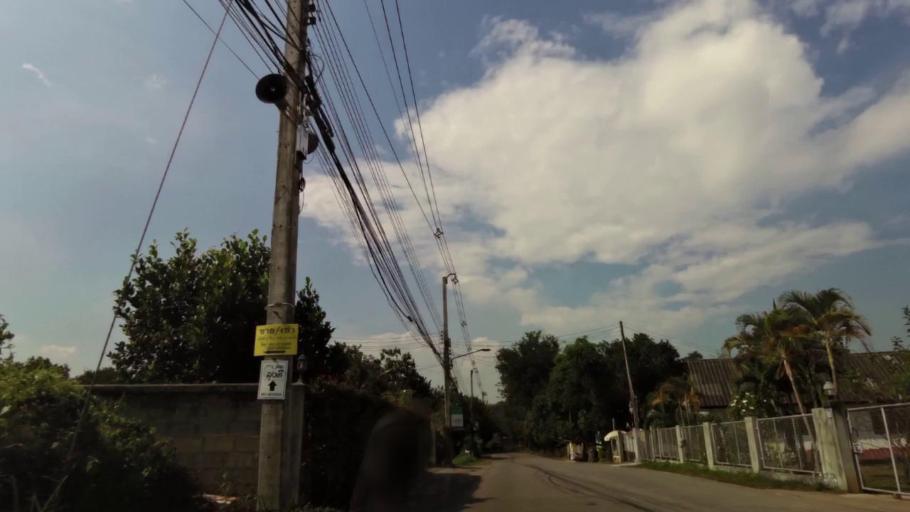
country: TH
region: Chiang Rai
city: Chiang Rai
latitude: 19.8886
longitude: 99.8167
